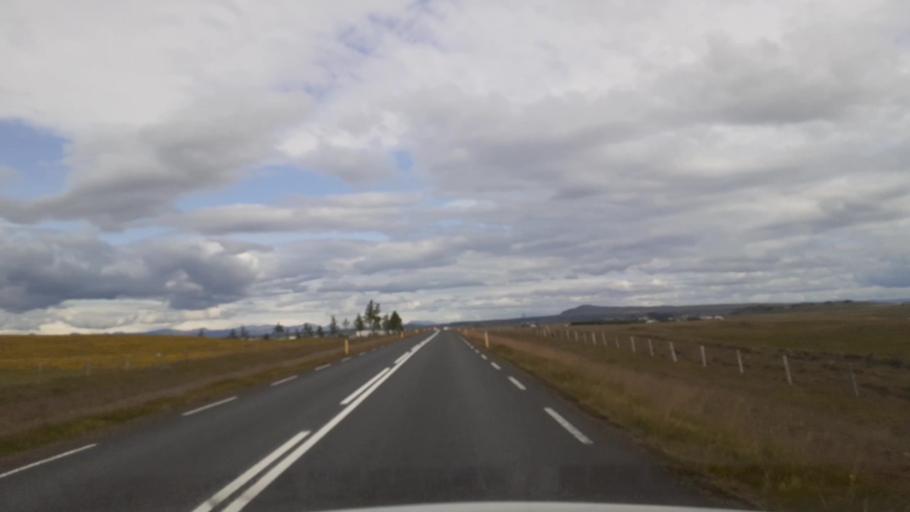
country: IS
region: South
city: Selfoss
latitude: 63.9299
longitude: -20.8460
